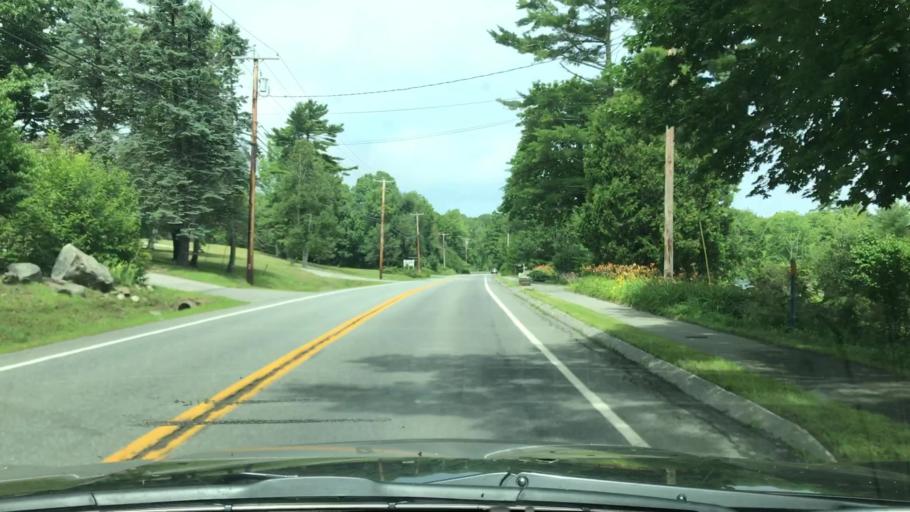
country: US
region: Maine
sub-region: Knox County
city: Camden
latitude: 44.2246
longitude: -69.0511
